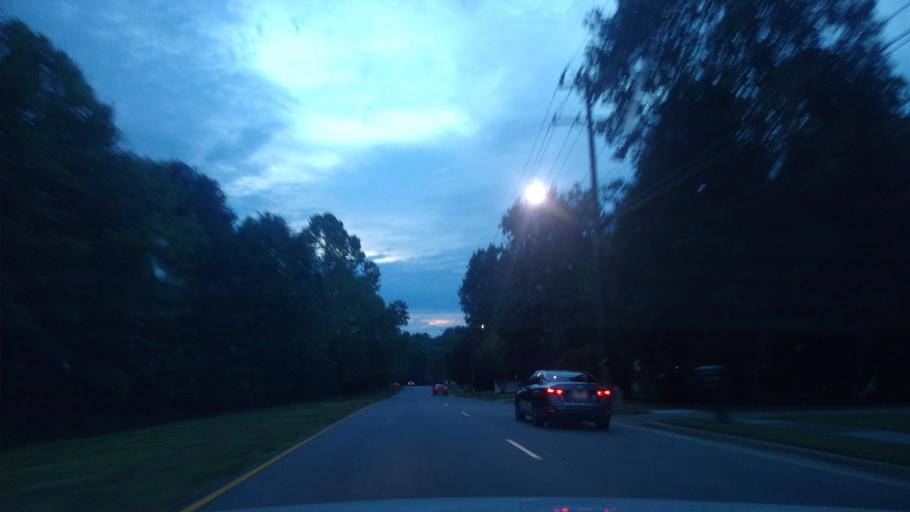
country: US
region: North Carolina
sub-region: Guilford County
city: Greensboro
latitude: 36.1069
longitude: -79.8054
